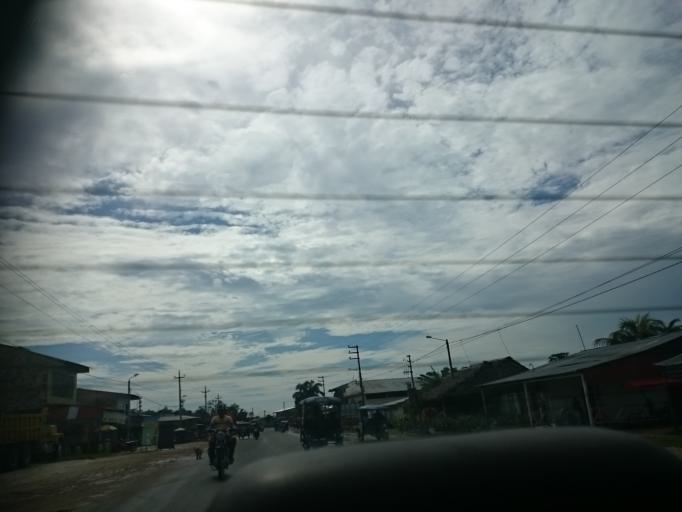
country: PE
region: Loreto
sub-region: Provincia de Maynas
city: Iquitos
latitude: -3.7951
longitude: -73.2997
